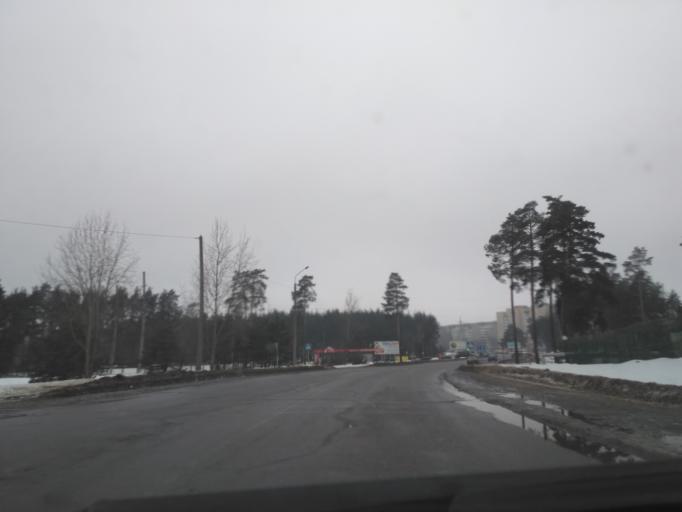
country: BY
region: Minsk
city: Horad Barysaw
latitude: 54.1999
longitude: 28.4857
